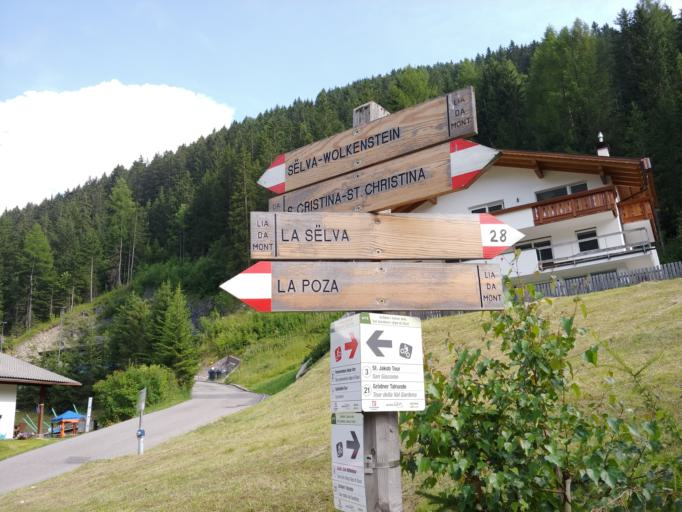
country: IT
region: Trentino-Alto Adige
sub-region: Bolzano
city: Santa Cristina Valgardena
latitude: 46.5569
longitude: 11.7433
